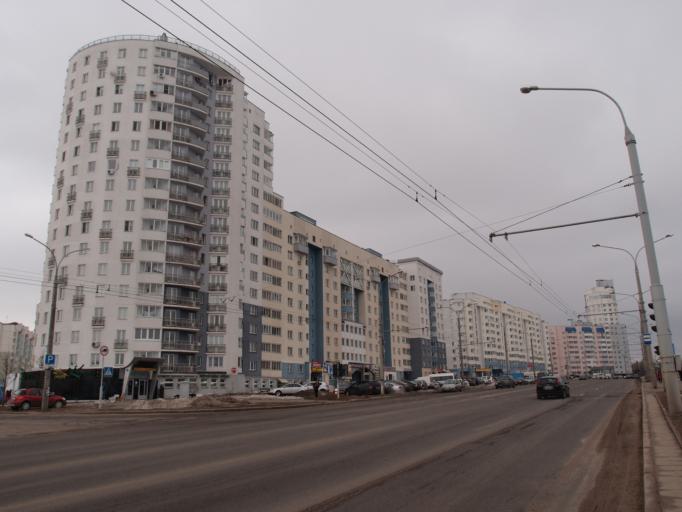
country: BY
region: Minsk
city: Syenitsa
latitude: 53.8426
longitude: 27.5728
